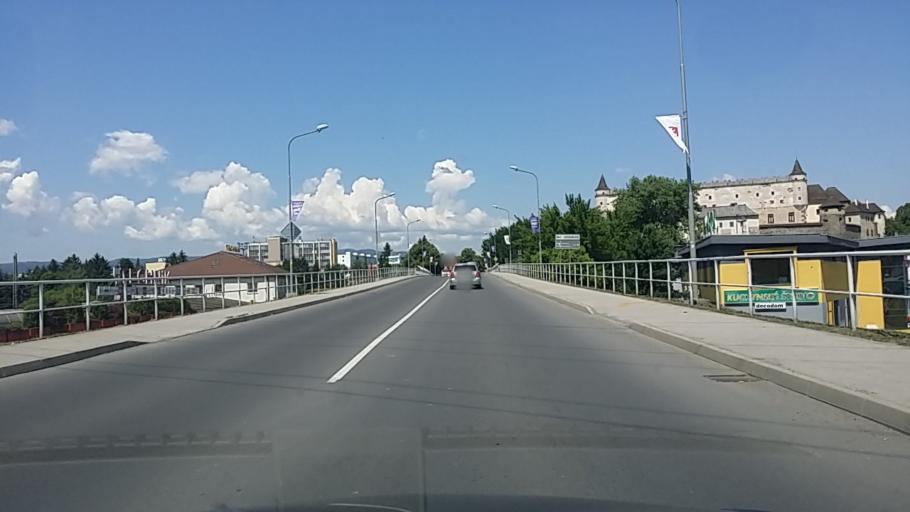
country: SK
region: Banskobystricky
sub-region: Okres Banska Bystrica
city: Zvolen
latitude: 48.5704
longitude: 19.1276
